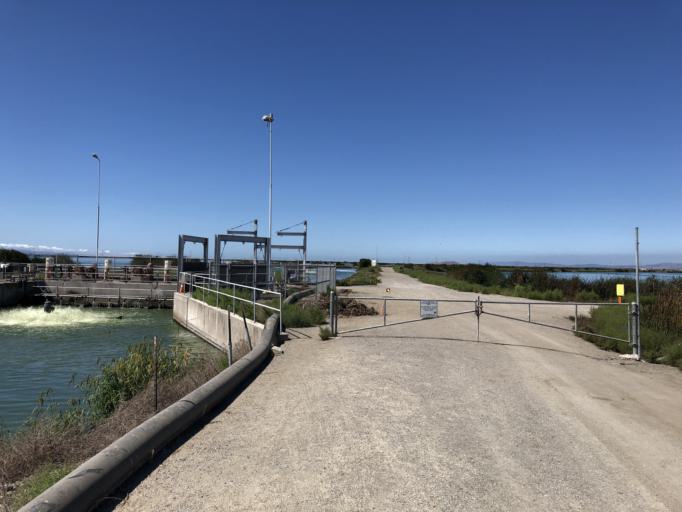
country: US
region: California
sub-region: Santa Clara County
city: Sunnyvale
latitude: 37.4248
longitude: -122.0158
